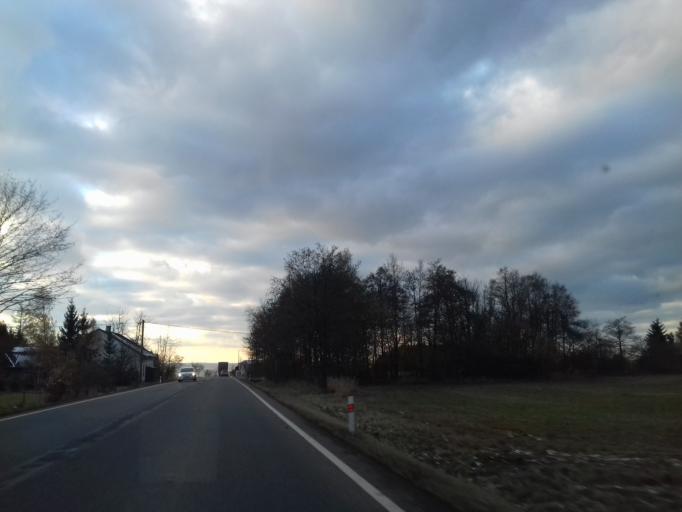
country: CZ
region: Pardubicky
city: Prosec
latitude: 49.7631
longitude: 16.1068
